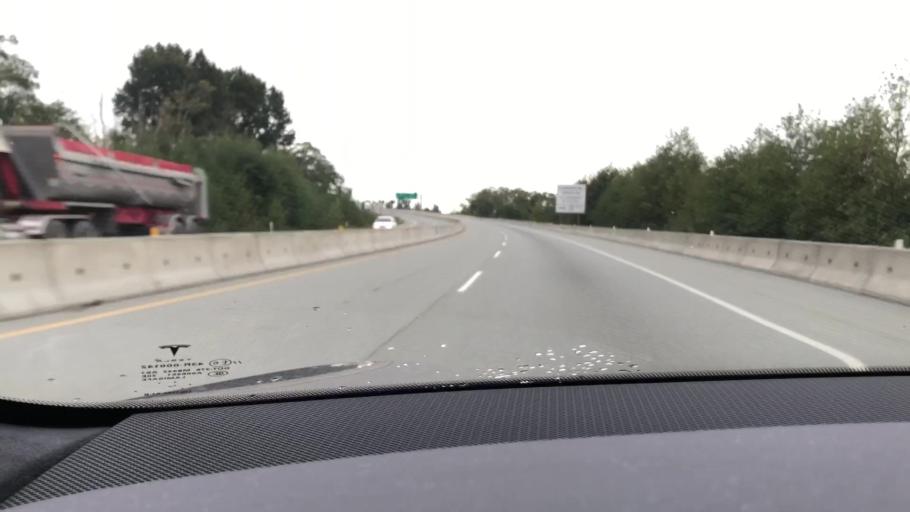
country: CA
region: British Columbia
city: Ladner
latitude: 49.1039
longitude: -123.0298
